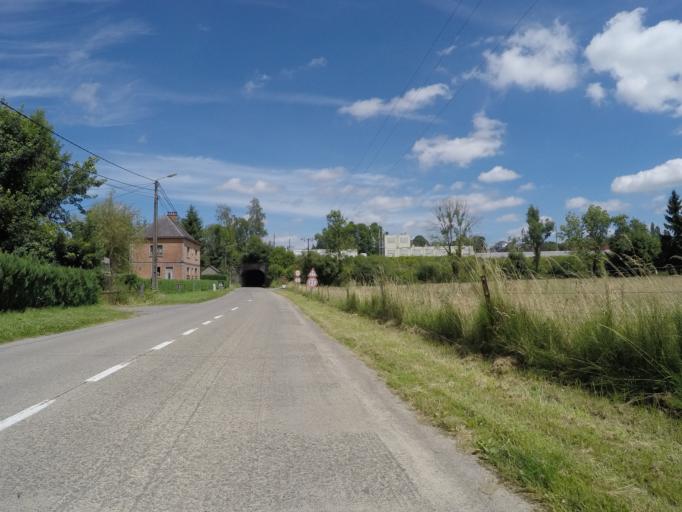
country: BE
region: Wallonia
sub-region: Province de Namur
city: Ciney
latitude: 50.2953
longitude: 5.0866
